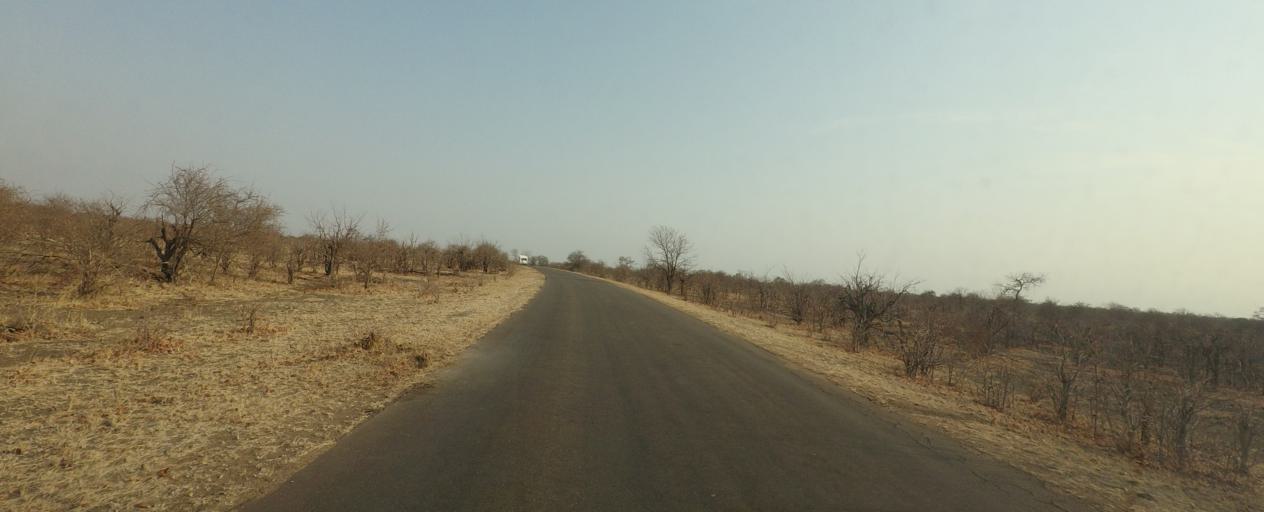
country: ZA
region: Limpopo
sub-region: Mopani District Municipality
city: Giyani
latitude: -23.0870
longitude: 31.4216
